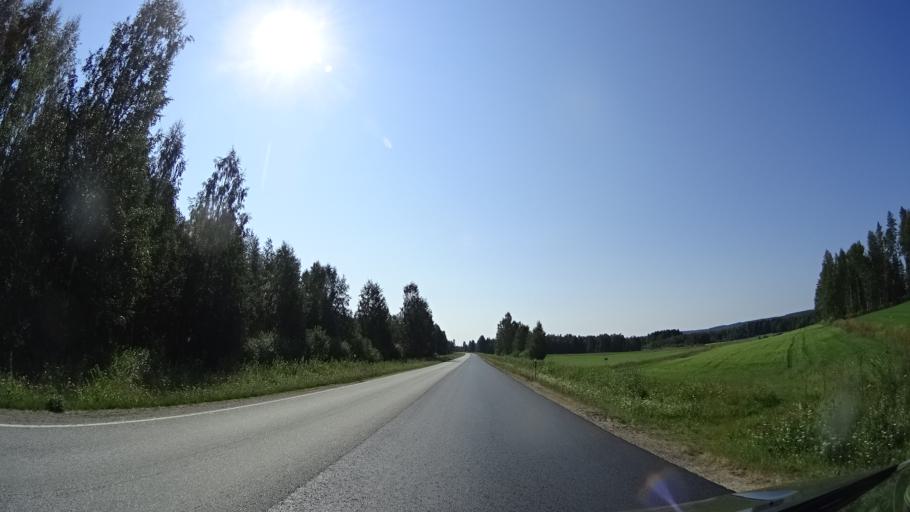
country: FI
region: North Karelia
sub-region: Joensuu
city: Juuka
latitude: 63.2165
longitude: 29.3030
